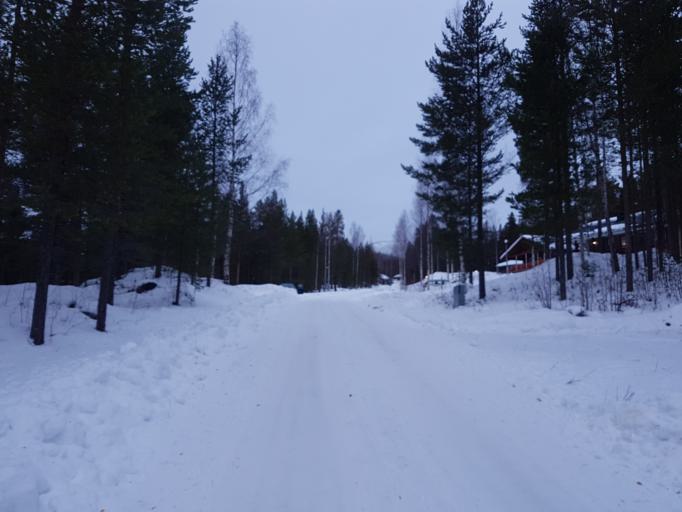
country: SE
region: Jaemtland
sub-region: Harjedalens Kommun
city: Sveg
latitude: 62.4199
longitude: 13.9493
